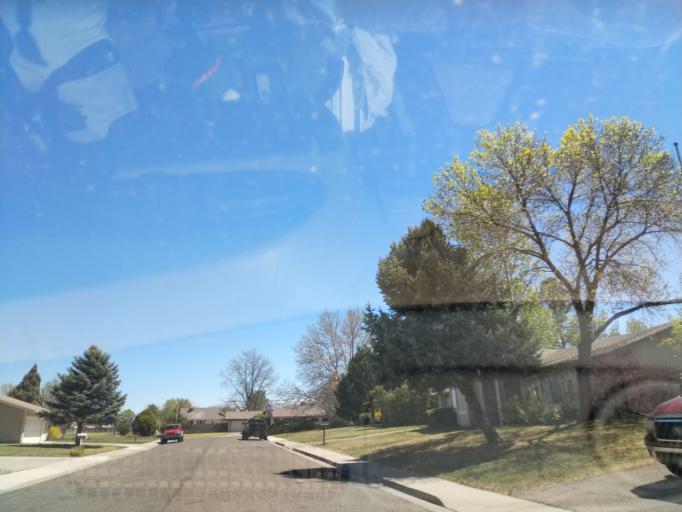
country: US
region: Colorado
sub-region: Mesa County
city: Grand Junction
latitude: 39.0929
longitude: -108.5399
